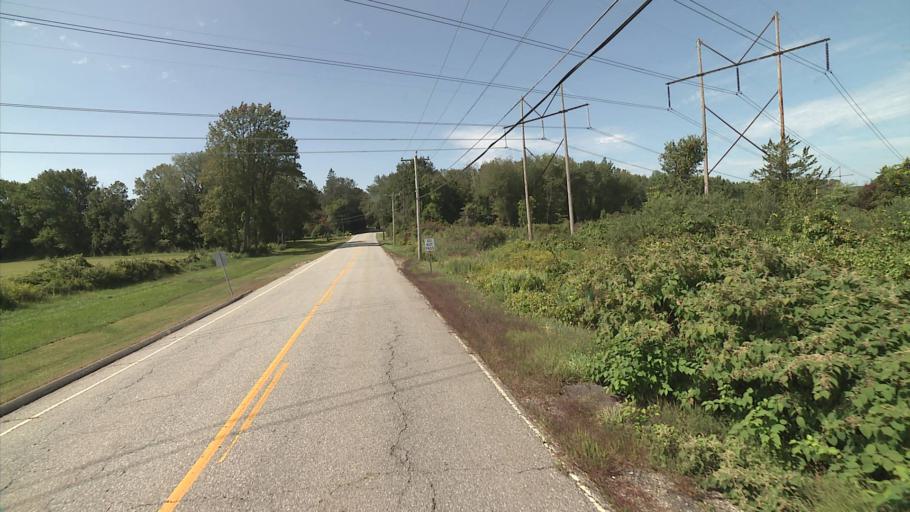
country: US
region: Connecticut
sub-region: Windham County
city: Willimantic
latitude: 41.6476
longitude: -72.2339
